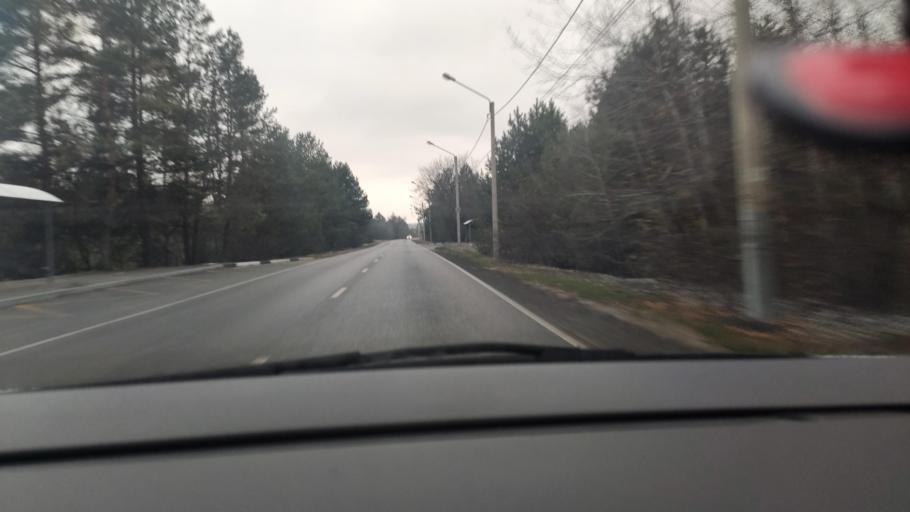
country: RU
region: Voronezj
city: Shilovo
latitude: 51.6079
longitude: 39.0440
